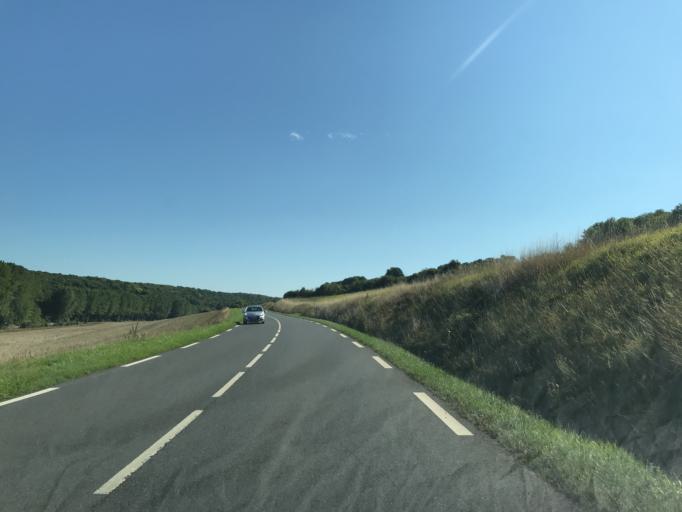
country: FR
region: Haute-Normandie
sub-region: Departement de l'Eure
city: Gasny
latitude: 49.1448
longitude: 1.6789
